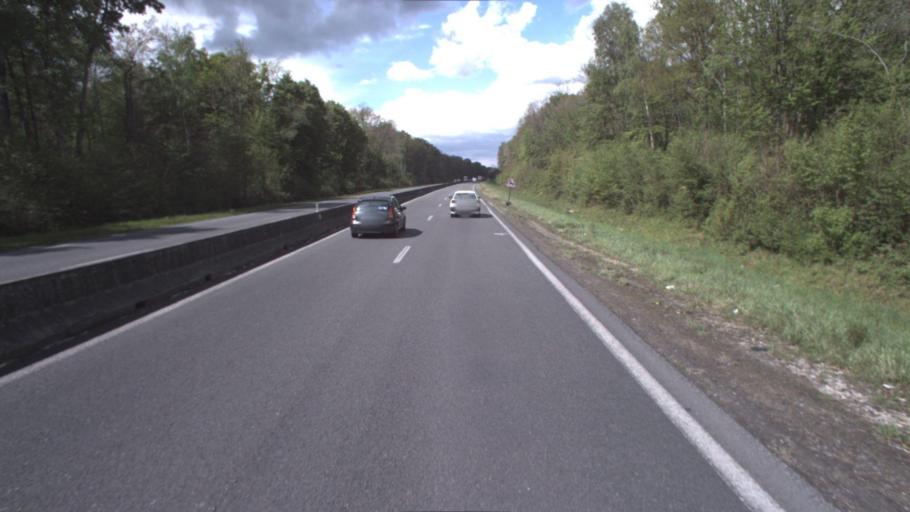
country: FR
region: Ile-de-France
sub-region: Departement de Seine-et-Marne
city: Ozoir-la-Ferriere
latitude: 48.7428
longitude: 2.6905
